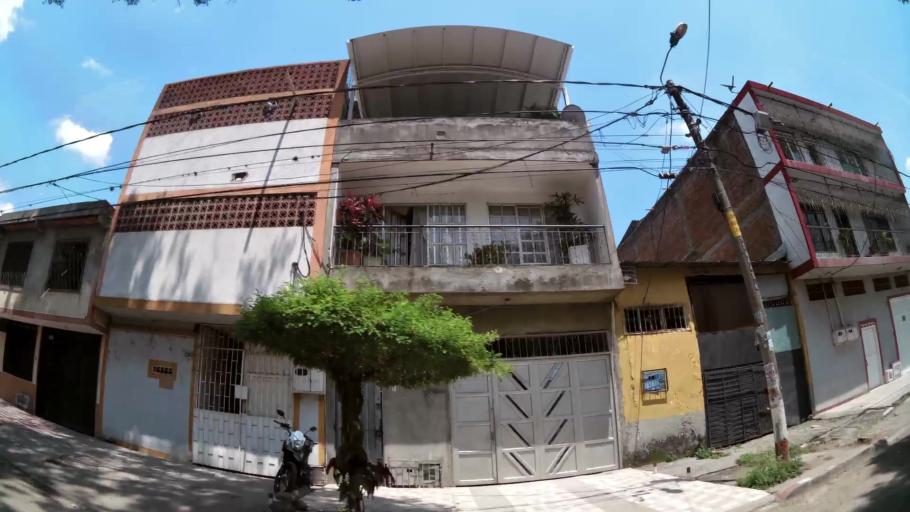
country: CO
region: Valle del Cauca
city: Cali
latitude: 3.4506
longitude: -76.5106
